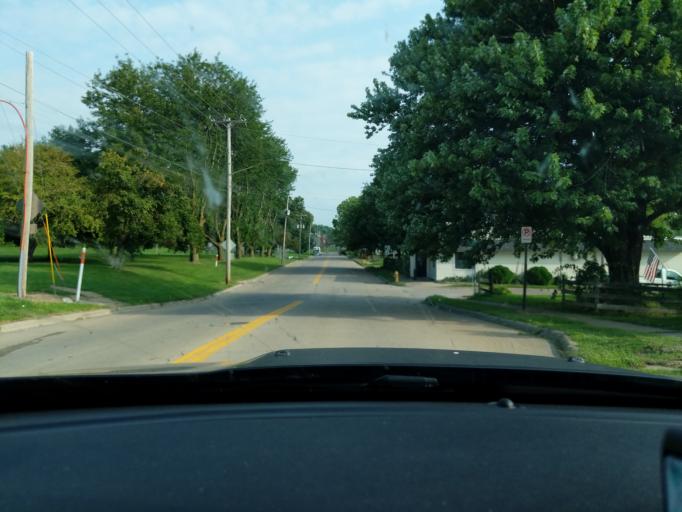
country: US
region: Illinois
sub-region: Rock Island County
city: Rock Island
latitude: 41.5029
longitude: -90.6243
